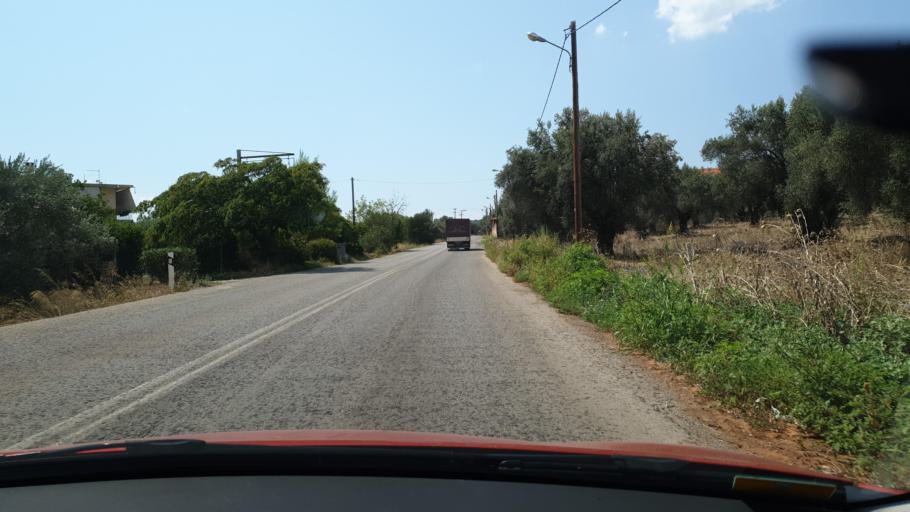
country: GR
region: Central Greece
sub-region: Nomos Evvoias
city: Psachna
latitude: 38.5812
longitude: 23.6165
